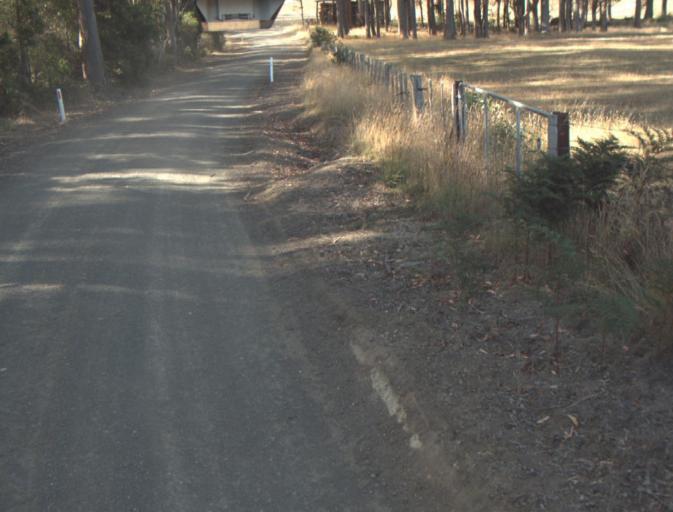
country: AU
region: Tasmania
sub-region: Dorset
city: Bridport
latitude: -41.1568
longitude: 147.2351
